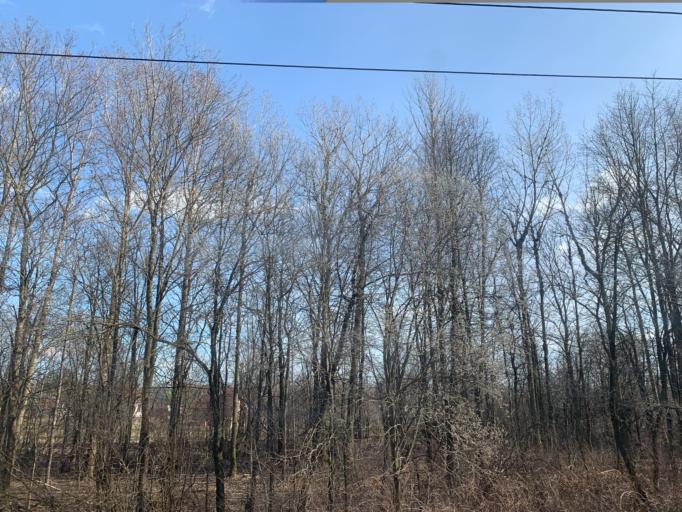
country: BY
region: Minsk
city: Stan'kava
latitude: 53.6926
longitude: 27.2356
